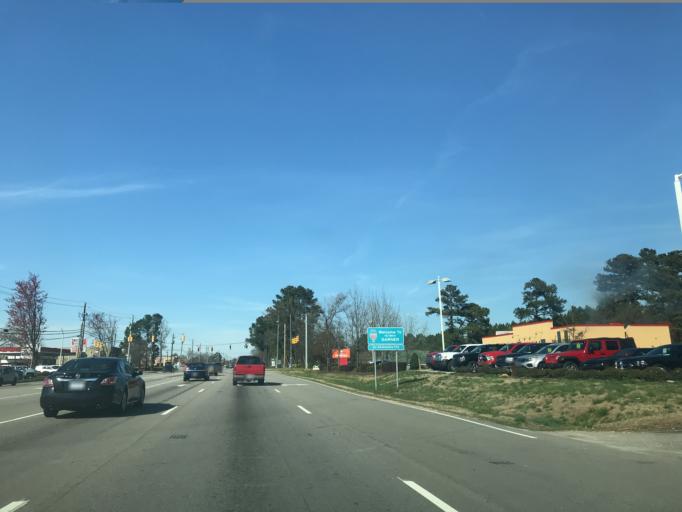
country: US
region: North Carolina
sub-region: Wake County
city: Garner
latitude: 35.7159
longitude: -78.6558
